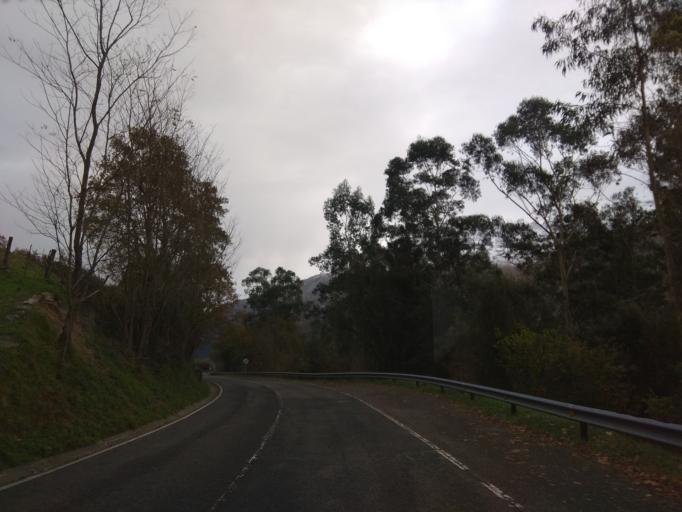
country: ES
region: Cantabria
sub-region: Provincia de Cantabria
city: Arredondo
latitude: 43.2798
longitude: -3.6243
